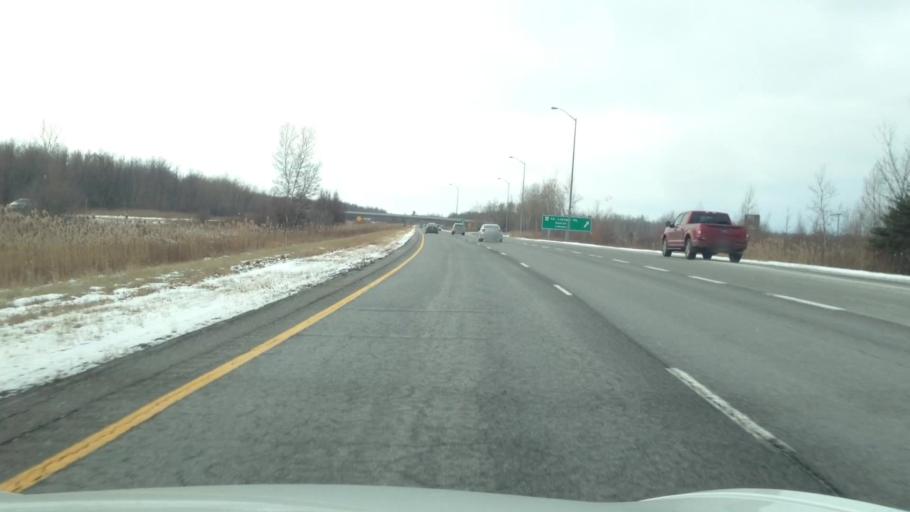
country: CA
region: Ontario
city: Bourget
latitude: 45.3144
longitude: -75.2343
